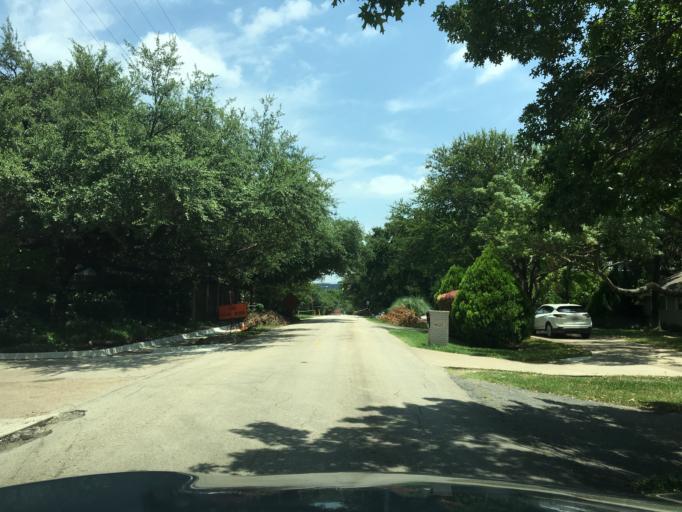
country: US
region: Texas
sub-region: Dallas County
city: Addison
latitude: 32.9134
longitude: -96.7933
